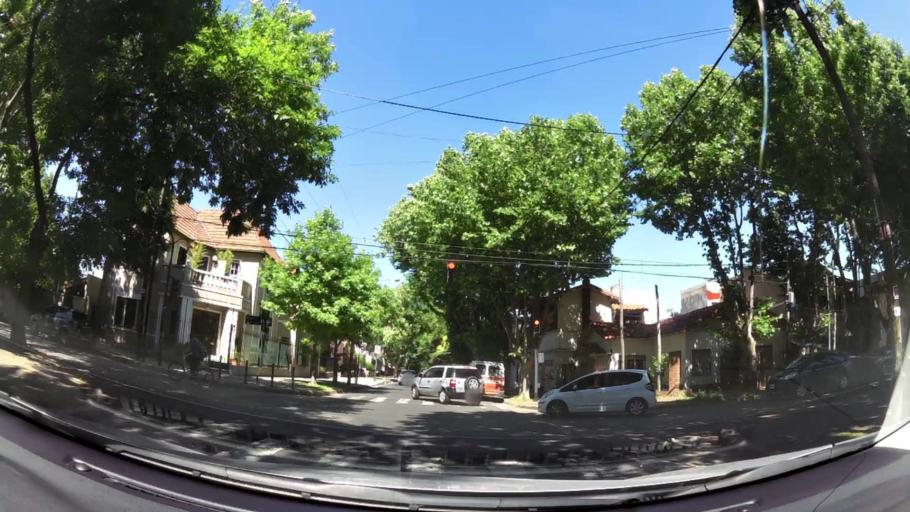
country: AR
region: Buenos Aires
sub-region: Partido de Vicente Lopez
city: Olivos
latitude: -34.5308
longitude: -58.4904
